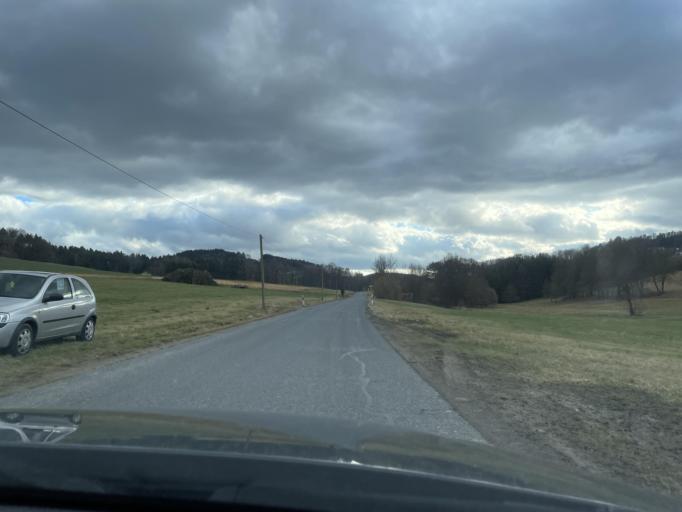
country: DE
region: Bavaria
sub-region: Upper Palatinate
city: Runding
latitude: 49.2293
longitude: 12.7727
